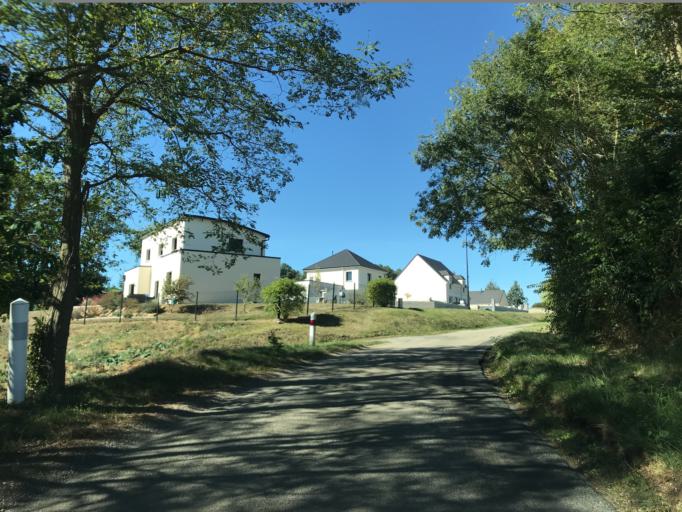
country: FR
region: Haute-Normandie
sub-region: Departement de l'Eure
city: Houlbec-Cocherel
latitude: 49.1007
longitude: 1.3360
